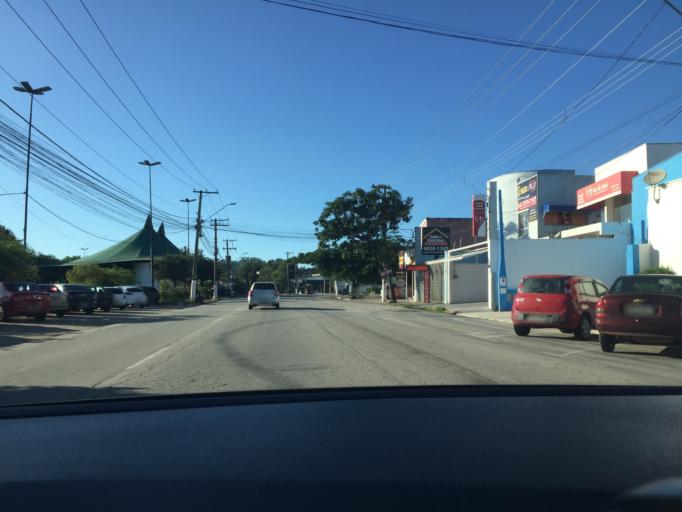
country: BR
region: Sao Paulo
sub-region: Campo Limpo Paulista
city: Campo Limpo Paulista
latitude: -23.2049
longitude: -46.7862
